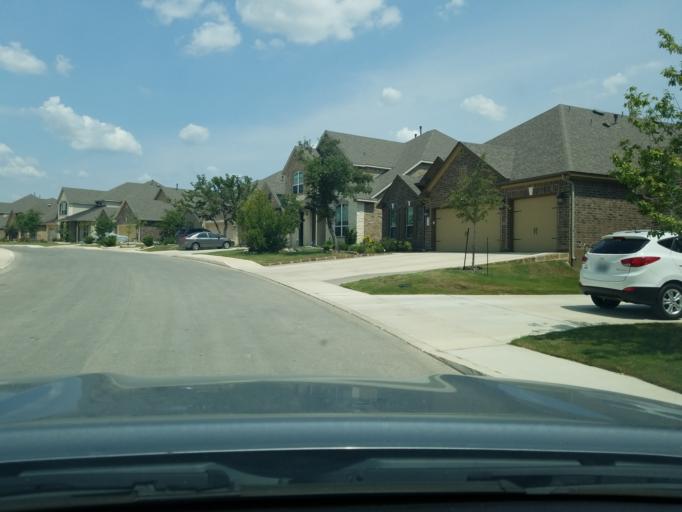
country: US
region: Texas
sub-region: Bexar County
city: Timberwood Park
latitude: 29.6820
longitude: -98.4806
